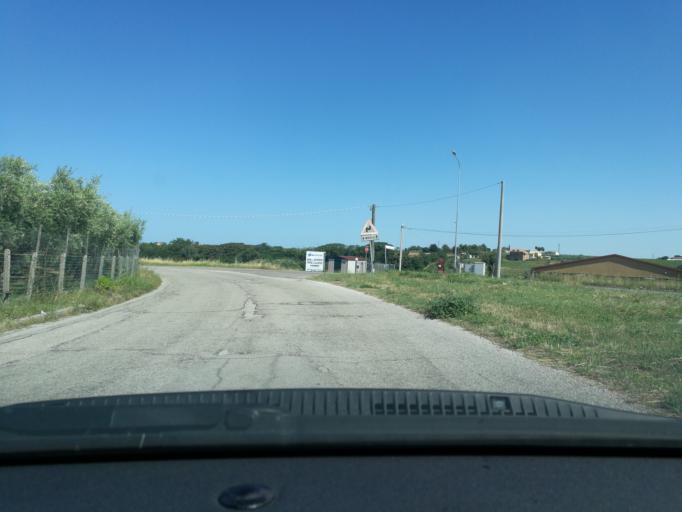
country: IT
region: Abruzzo
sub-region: Provincia di Chieti
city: Vasto
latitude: 42.1665
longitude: 14.6922
